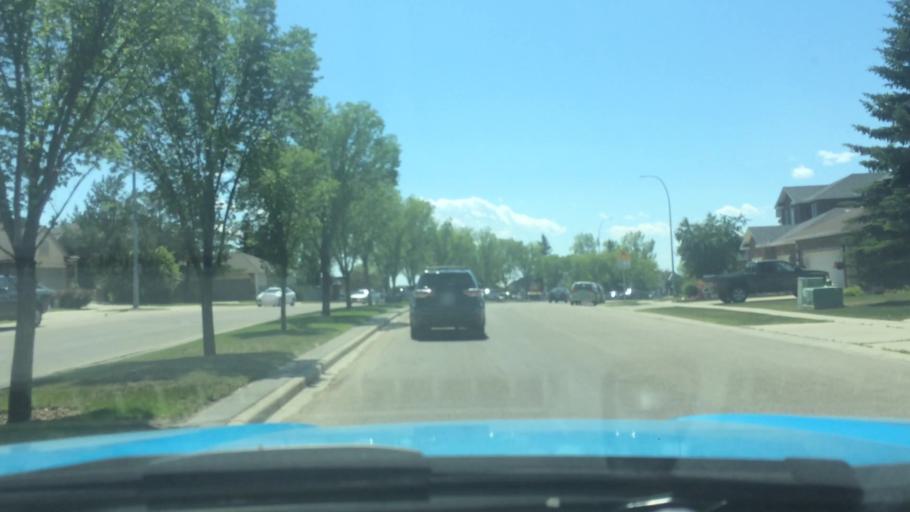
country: CA
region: Alberta
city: Calgary
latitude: 51.1347
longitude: -114.2020
